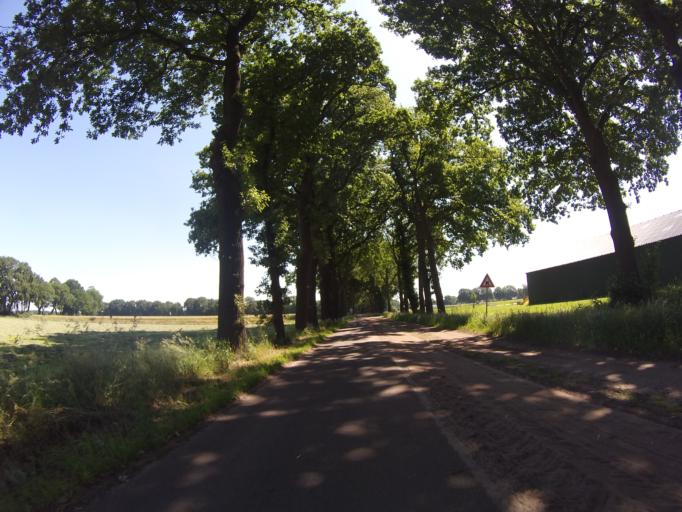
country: NL
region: Drenthe
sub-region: Gemeente Coevorden
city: Sleen
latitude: 52.7624
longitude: 6.8271
